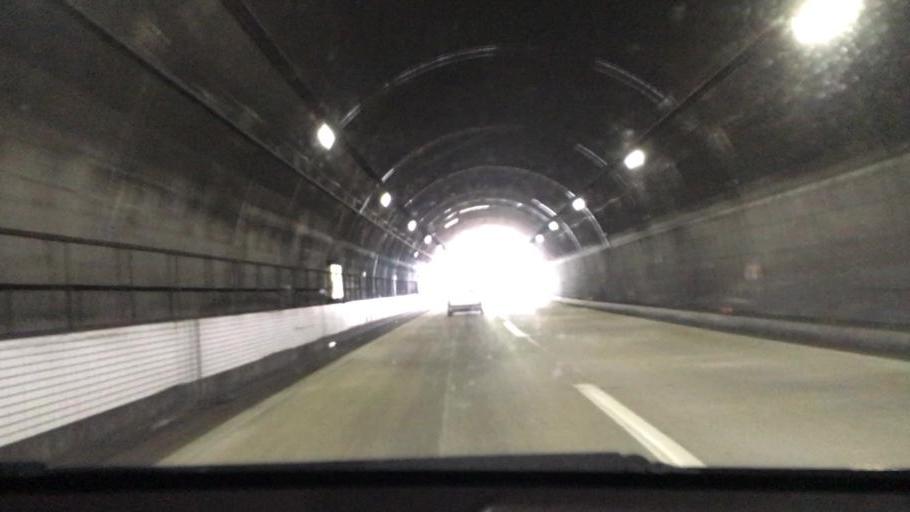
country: JP
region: Yamaguchi
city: Tokuyama
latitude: 34.0685
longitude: 131.7059
